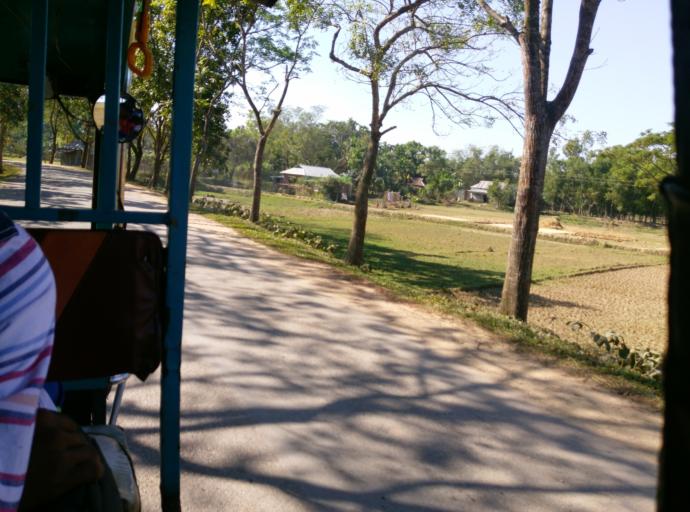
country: BD
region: Dhaka
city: Netrakona
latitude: 25.0660
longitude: 90.4995
